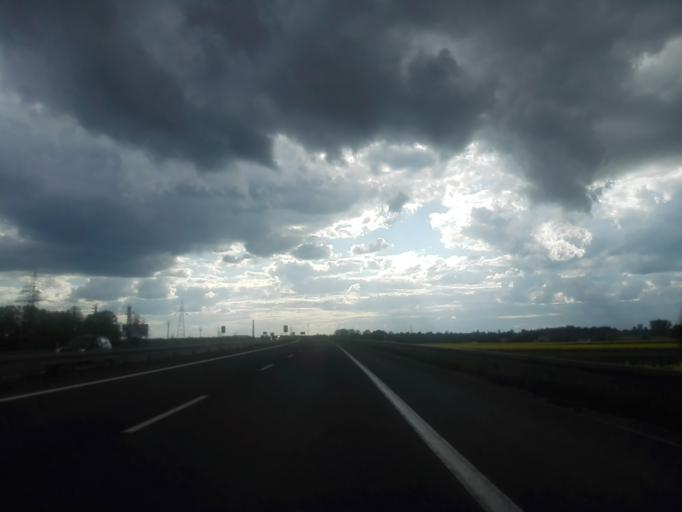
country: PL
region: Masovian Voivodeship
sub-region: Powiat ostrowski
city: Ostrow Mazowiecka
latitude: 52.8207
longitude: 21.9071
